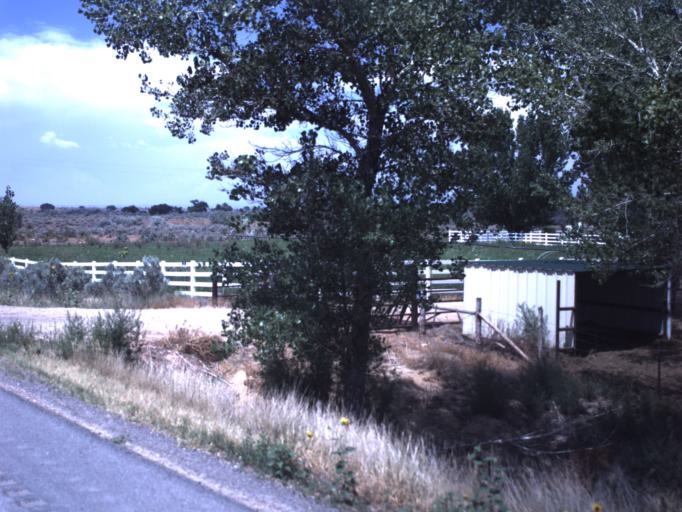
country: US
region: Utah
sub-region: Duchesne County
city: Roosevelt
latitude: 40.3030
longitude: -109.7875
